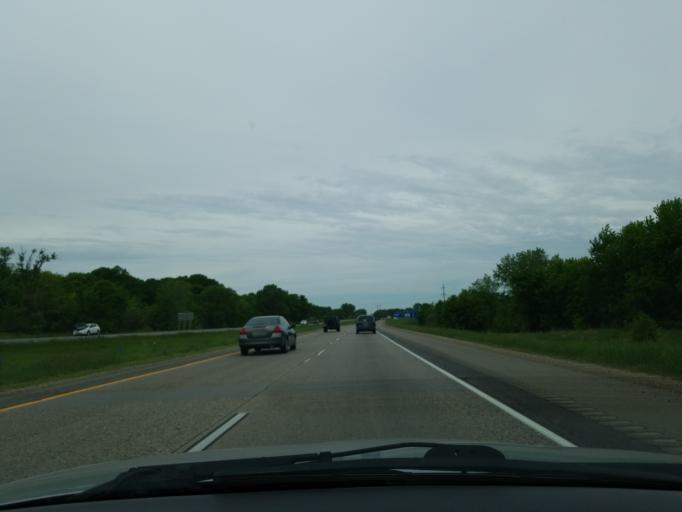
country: US
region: Minnesota
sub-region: Sherburne County
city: Big Lake
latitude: 45.2799
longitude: -93.7442
